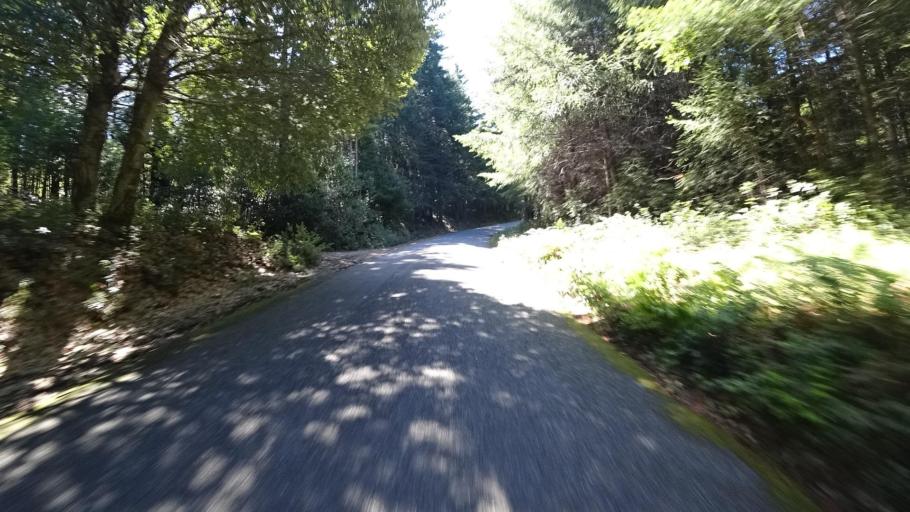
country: US
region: California
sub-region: Humboldt County
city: Redway
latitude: 40.1750
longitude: -124.0891
